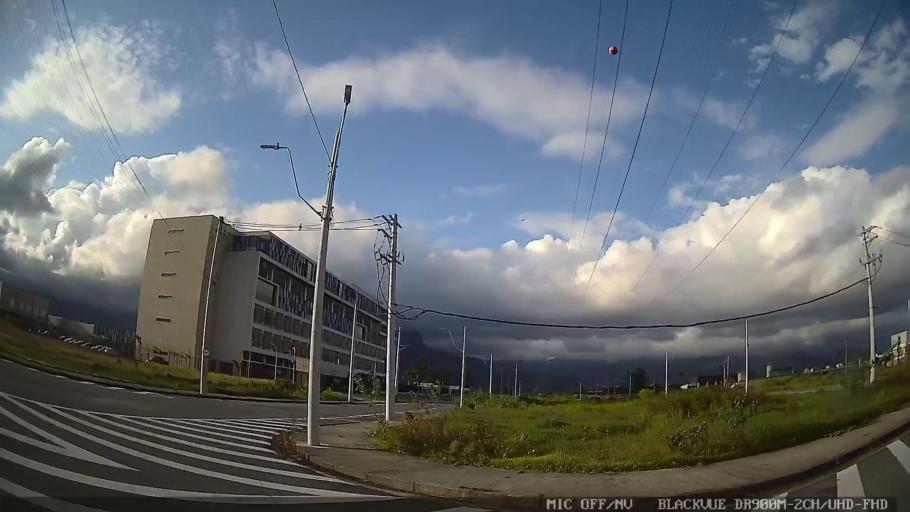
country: BR
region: Sao Paulo
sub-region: Caraguatatuba
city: Caraguatatuba
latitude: -23.6588
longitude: -45.4398
